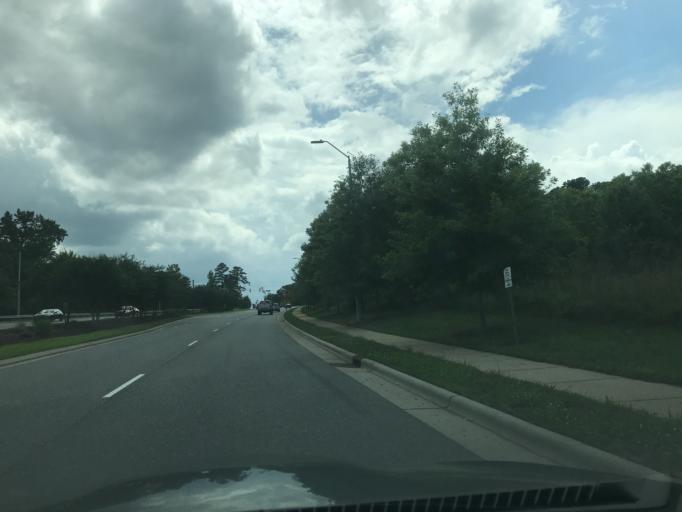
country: US
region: North Carolina
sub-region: Wake County
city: Wake Forest
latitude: 35.9360
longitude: -78.5745
